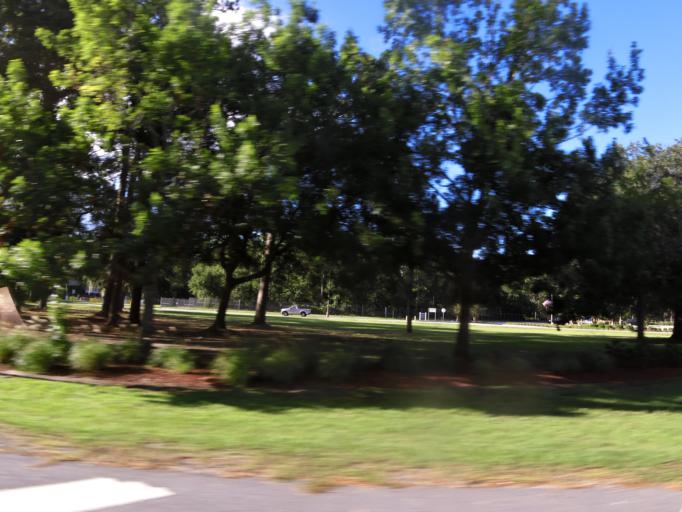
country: US
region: Georgia
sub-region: Glynn County
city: Country Club Estates
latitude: 31.2275
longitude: -81.4637
